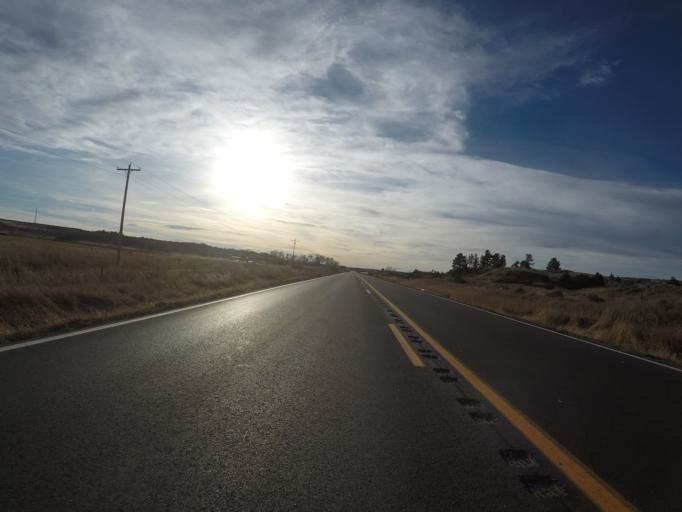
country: US
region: Montana
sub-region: Musselshell County
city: Roundup
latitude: 46.3700
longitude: -108.6456
